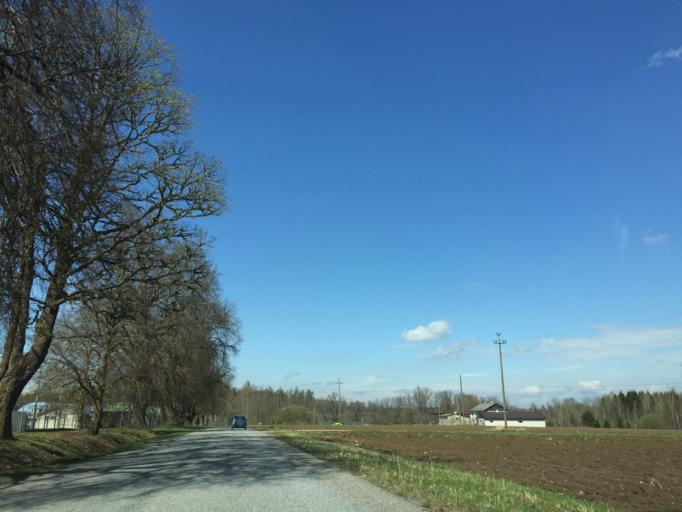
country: EE
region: Tartu
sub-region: Elva linn
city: Elva
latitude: 58.1484
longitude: 26.2332
